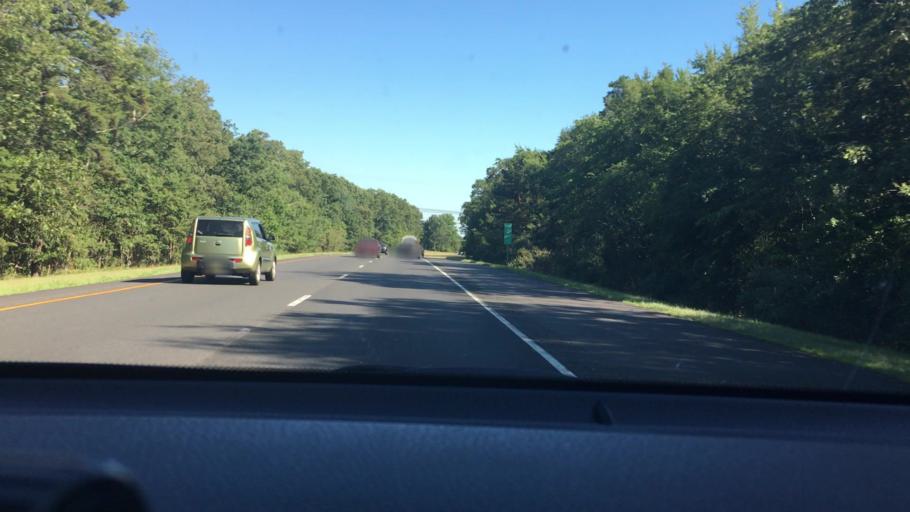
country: US
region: New Jersey
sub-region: Gloucester County
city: Clayton
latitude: 39.6305
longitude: -75.0934
